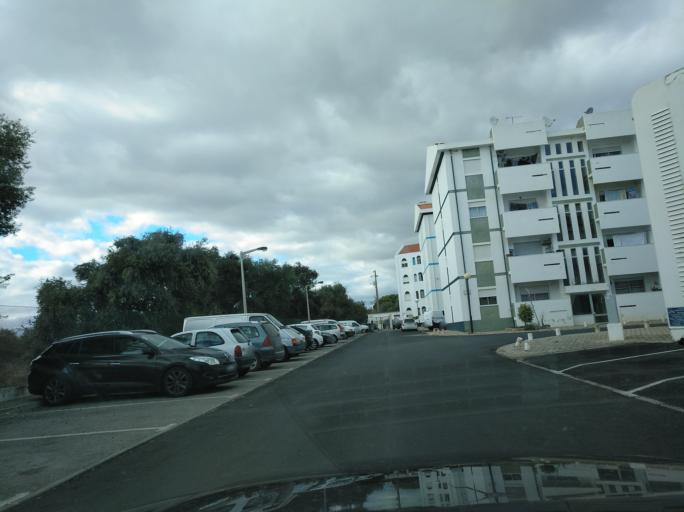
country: PT
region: Faro
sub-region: Tavira
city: Luz
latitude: 37.0926
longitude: -7.7052
